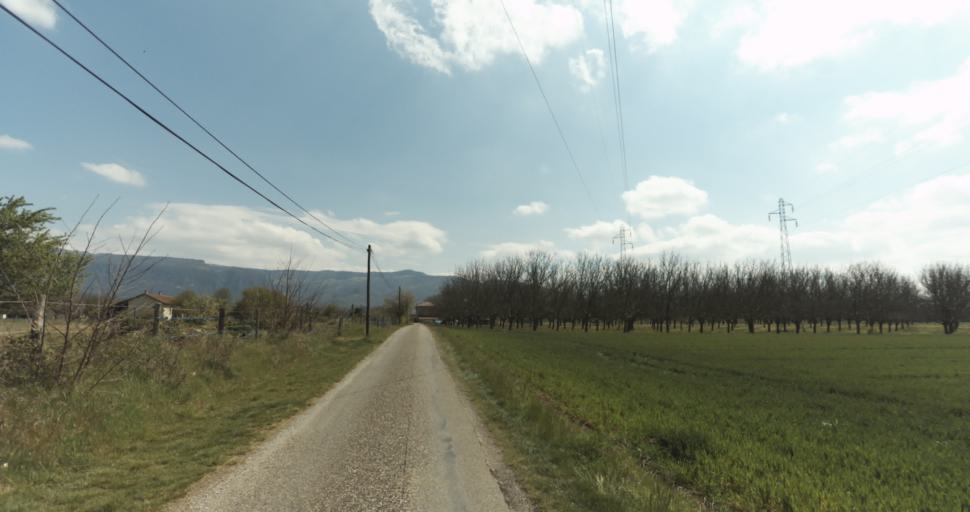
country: FR
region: Rhone-Alpes
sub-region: Departement de l'Isere
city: Saint-Marcellin
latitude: 45.1376
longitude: 5.3132
